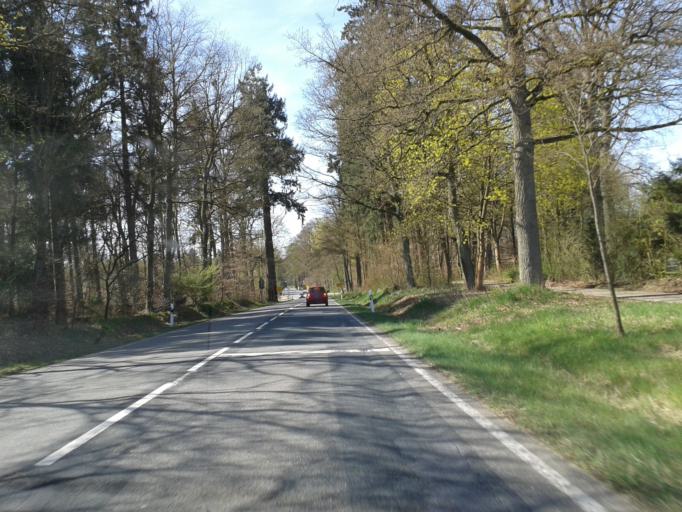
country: DE
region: Lower Saxony
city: Fassberg
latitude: 52.9608
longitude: 10.1884
